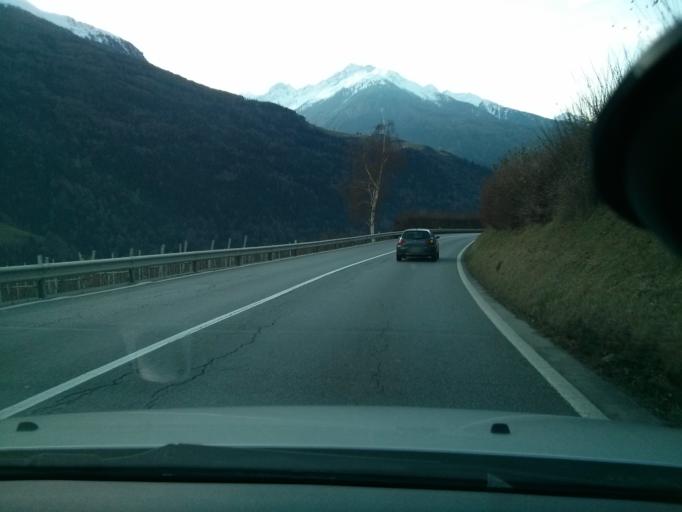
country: IT
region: Trentino-Alto Adige
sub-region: Bolzano
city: Lasa
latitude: 46.6177
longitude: 10.7321
